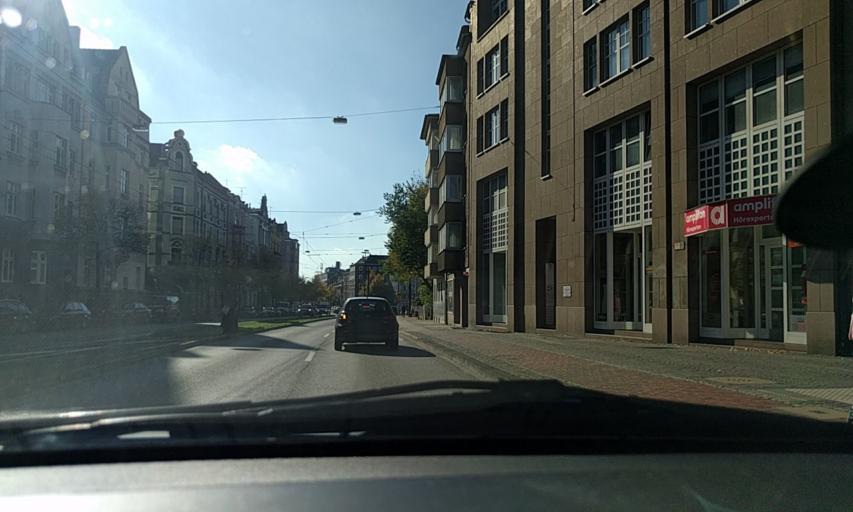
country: DE
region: North Rhine-Westphalia
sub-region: Regierungsbezirk Dusseldorf
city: Dusseldorf
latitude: 51.2159
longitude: 6.8028
